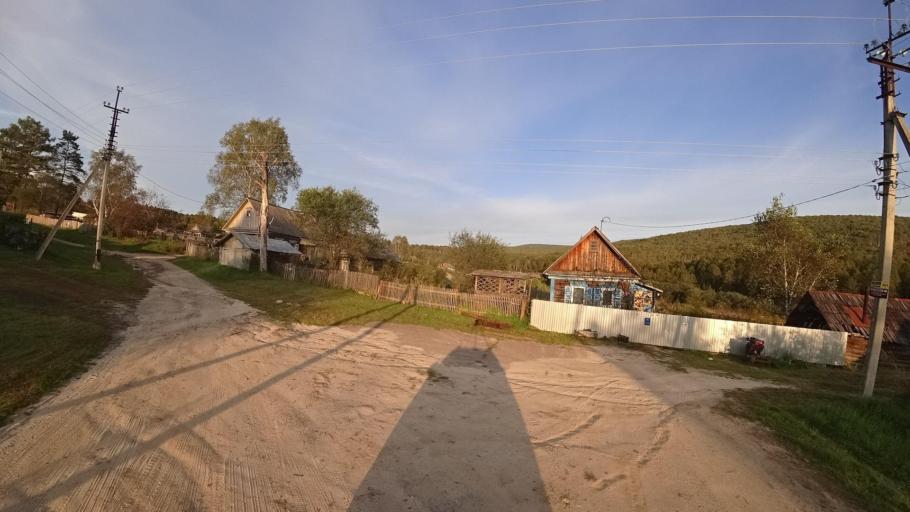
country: RU
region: Jewish Autonomous Oblast
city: Kul'dur
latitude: 49.2076
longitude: 131.6459
